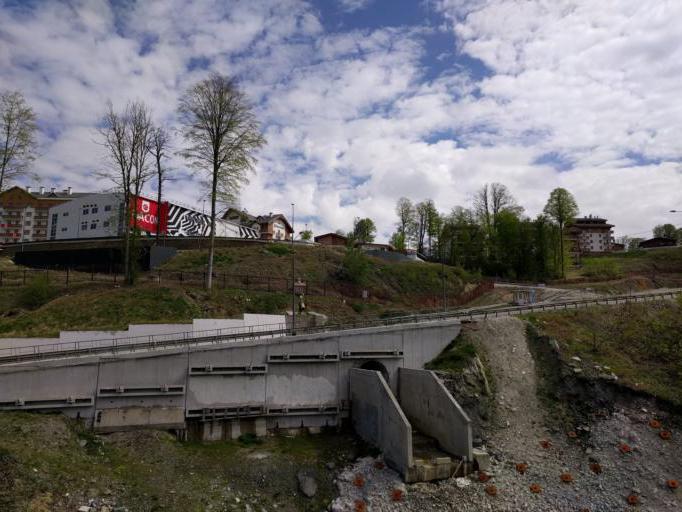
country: RU
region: Krasnodarskiy
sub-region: Sochi City
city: Krasnaya Polyana
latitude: 43.6618
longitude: 40.3140
